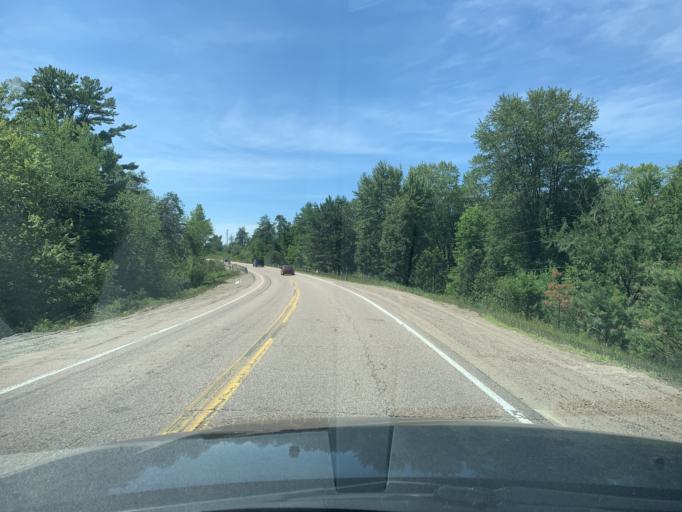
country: CA
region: Ontario
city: Petawawa
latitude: 45.6658
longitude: -77.5762
